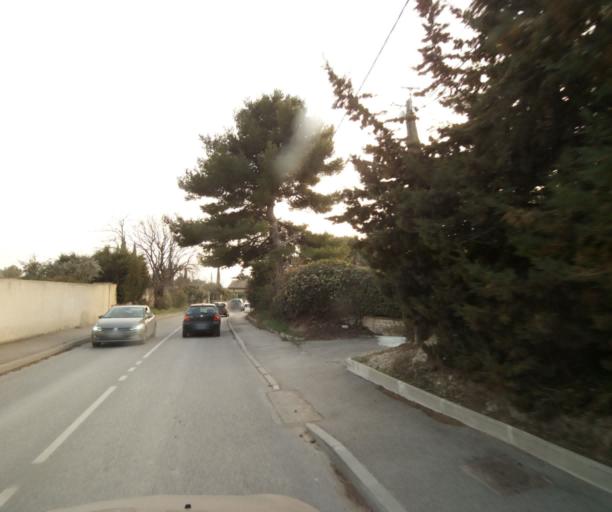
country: FR
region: Provence-Alpes-Cote d'Azur
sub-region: Departement des Bouches-du-Rhone
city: Eguilles
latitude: 43.5726
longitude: 5.3613
